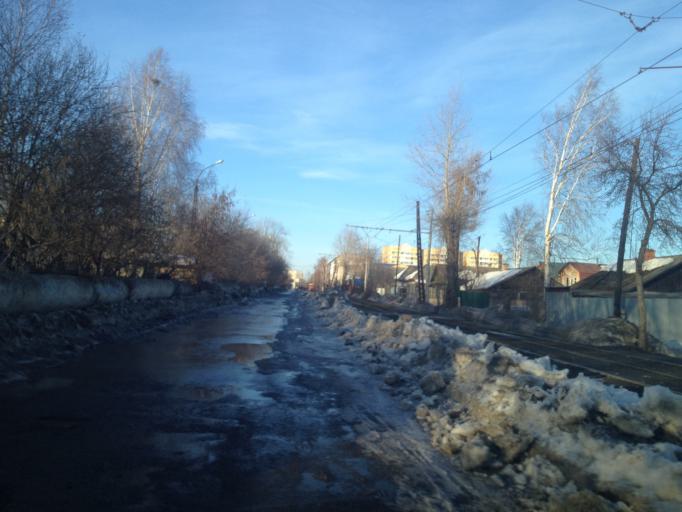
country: RU
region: Sverdlovsk
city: Sovkhoznyy
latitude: 56.7669
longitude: 60.5944
